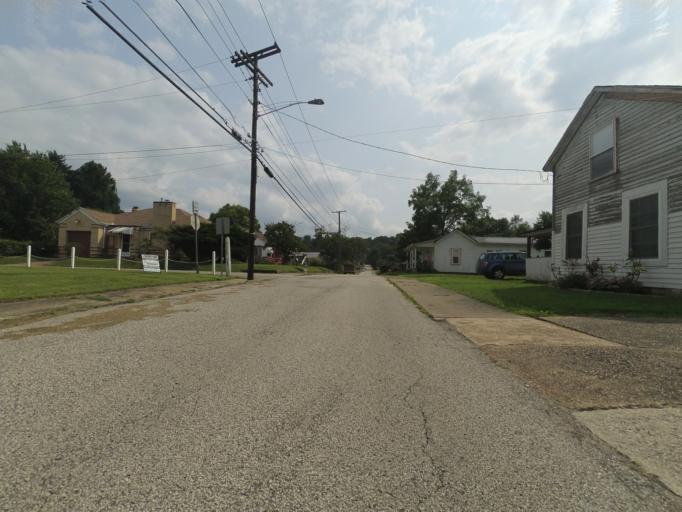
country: US
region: West Virginia
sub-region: Cabell County
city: Huntington
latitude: 38.4032
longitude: -82.4061
